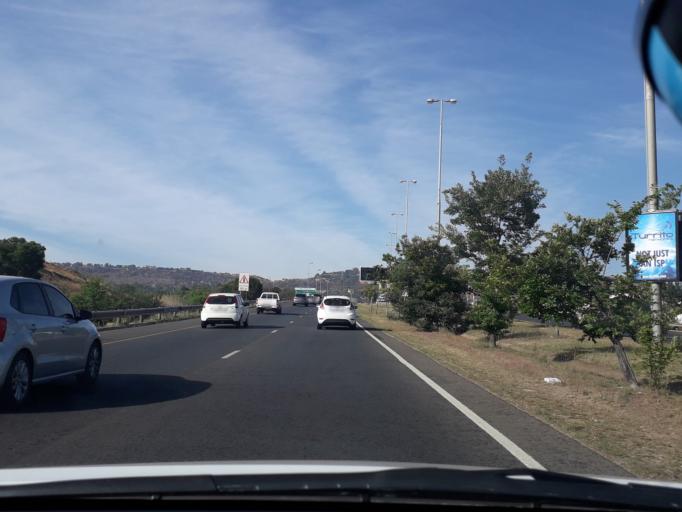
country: ZA
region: Gauteng
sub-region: City of Johannesburg Metropolitan Municipality
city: Roodepoort
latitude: -26.1233
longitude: 27.9110
